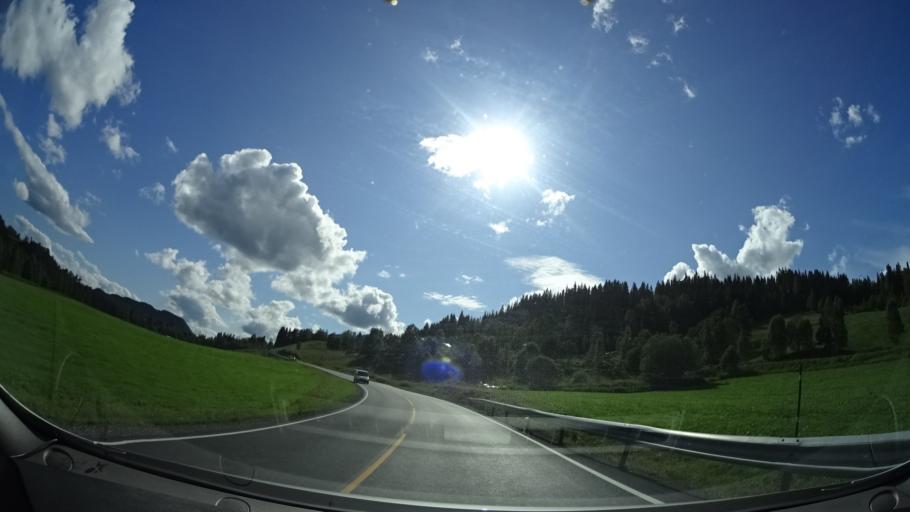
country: NO
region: Sor-Trondelag
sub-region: Snillfjord
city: Krokstadora
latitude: 63.2453
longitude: 9.6019
